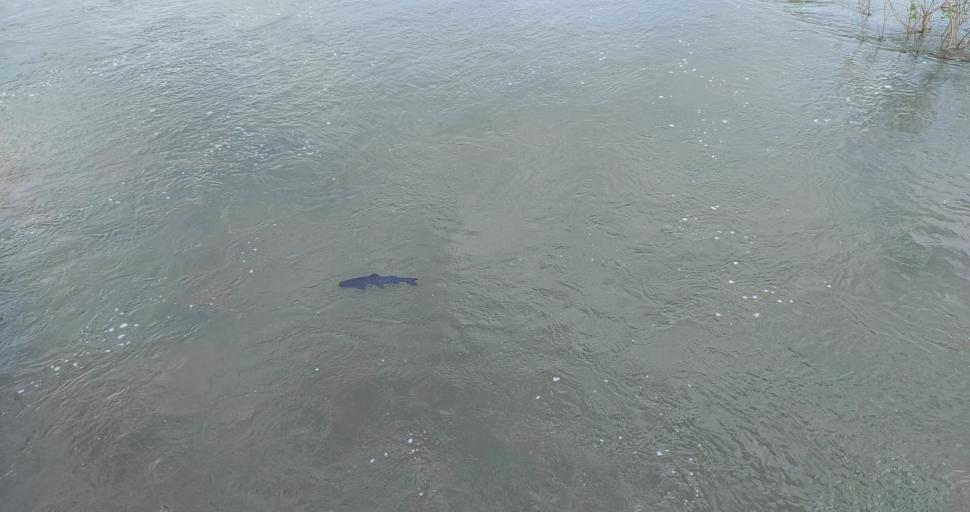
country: AR
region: Misiones
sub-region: Departamento de Iguazu
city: Puerto Iguazu
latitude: -25.6971
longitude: -54.4393
